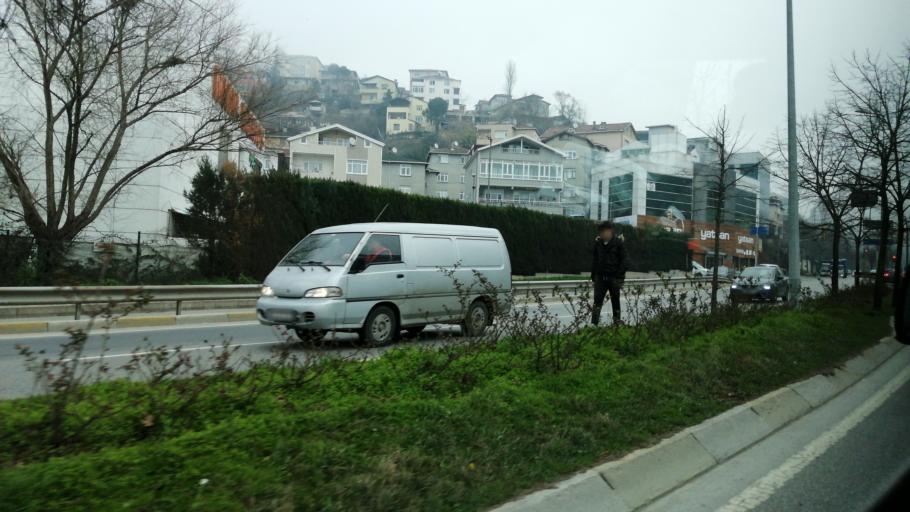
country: TR
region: Istanbul
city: Umraniye
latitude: 41.0806
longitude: 29.0795
